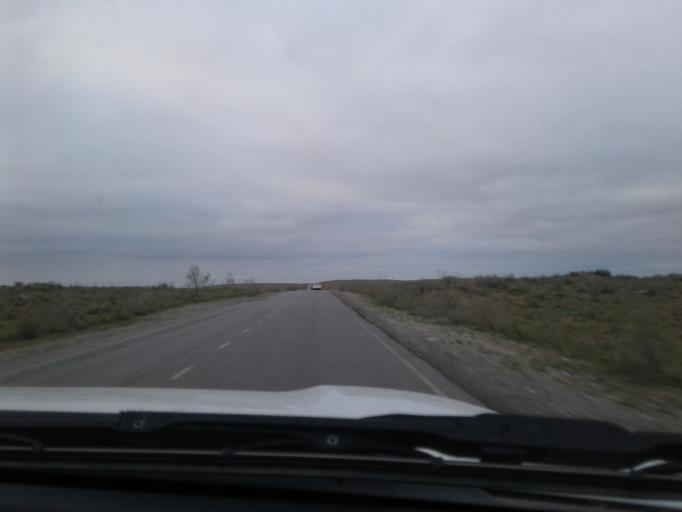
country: TM
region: Lebap
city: Turkmenabat
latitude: 39.0685
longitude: 63.7368
